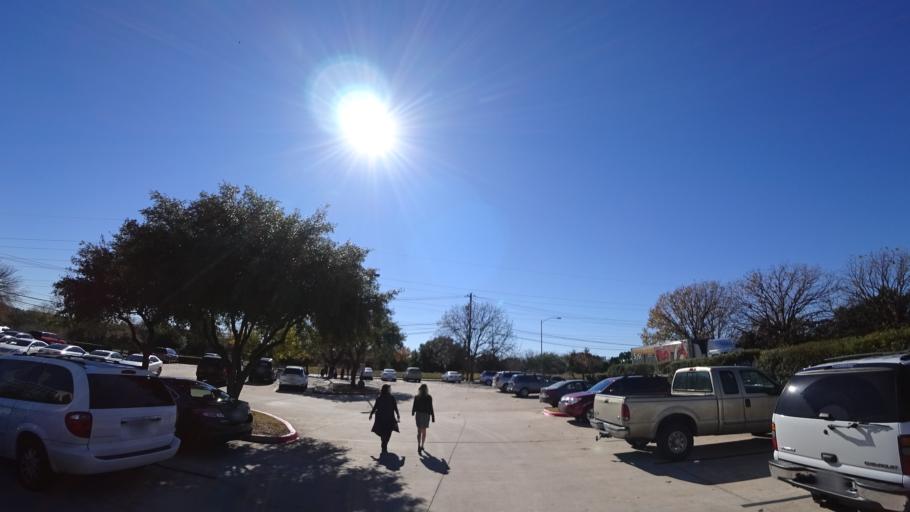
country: US
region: Texas
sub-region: Travis County
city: Wells Branch
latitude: 30.4094
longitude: -97.7056
